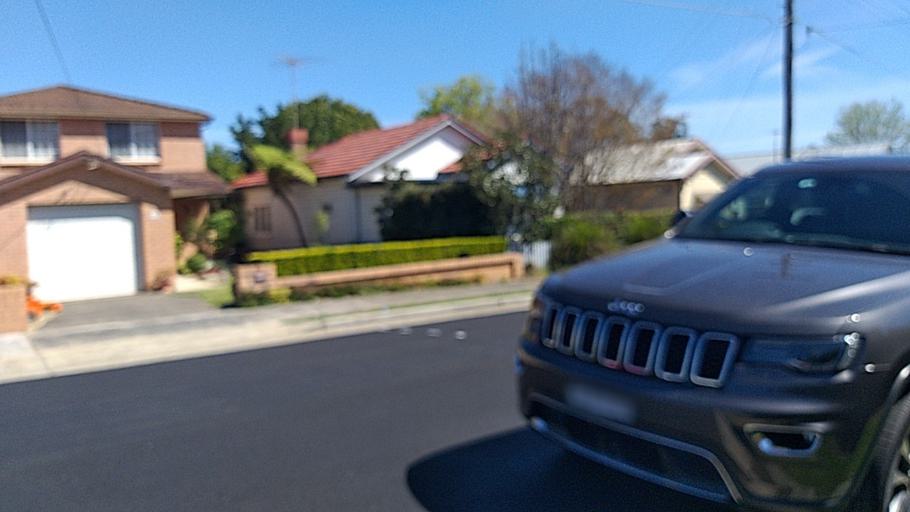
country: AU
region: New South Wales
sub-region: Hunters Hill
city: Gladesville
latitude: -33.8240
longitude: 151.1195
